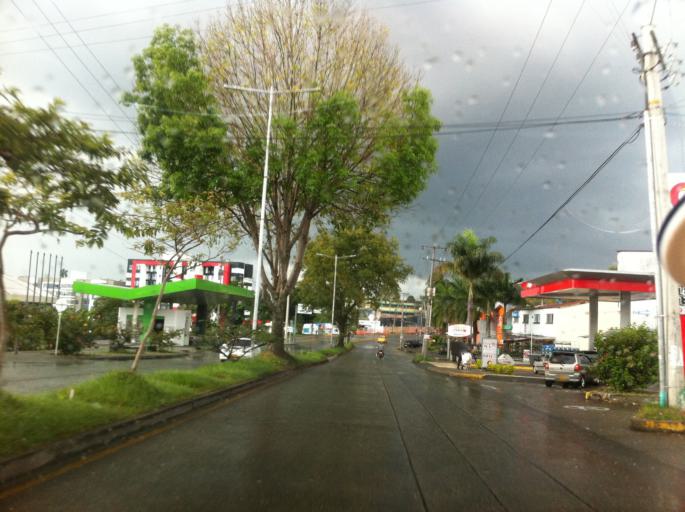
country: CO
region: Quindio
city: Armenia
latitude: 4.5471
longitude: -75.6670
